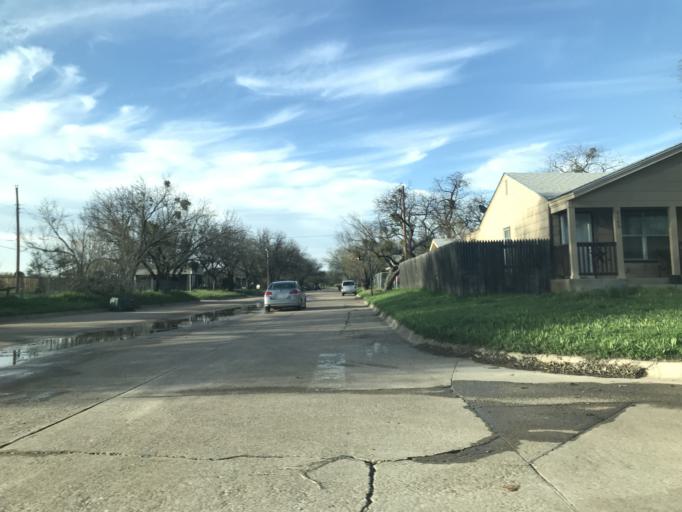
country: US
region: Texas
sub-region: Taylor County
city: Abilene
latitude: 32.4341
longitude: -99.7615
